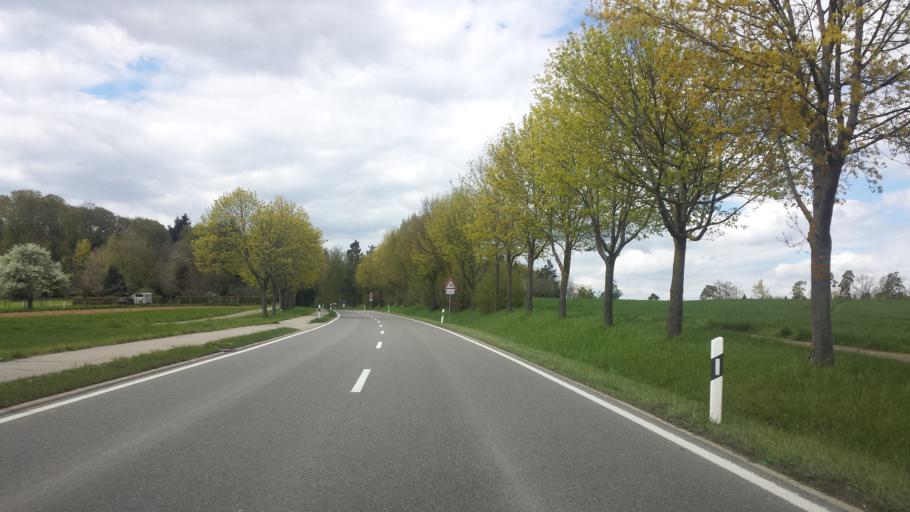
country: DE
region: Baden-Wuerttemberg
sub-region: Regierungsbezirk Stuttgart
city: Rutesheim
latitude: 48.8186
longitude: 8.9362
